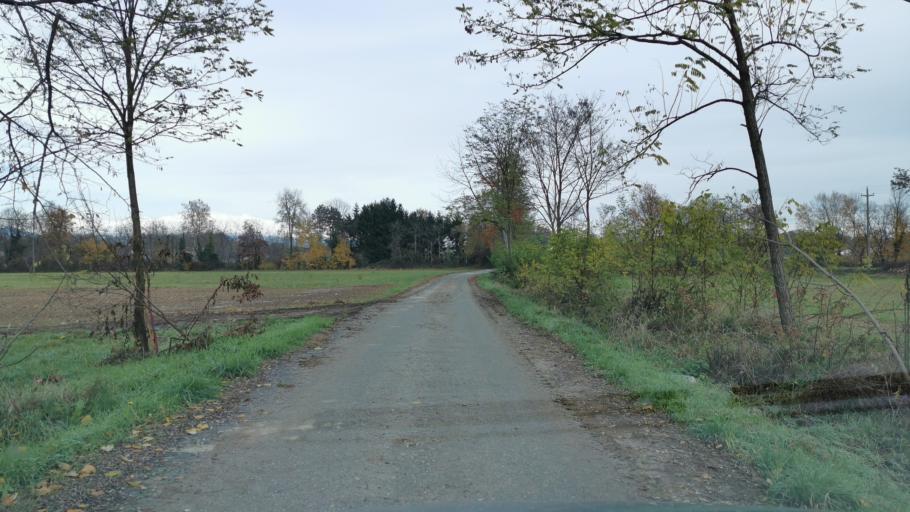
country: IT
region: Piedmont
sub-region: Provincia di Torino
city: San Francesco al Campo
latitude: 45.2115
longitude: 7.6768
